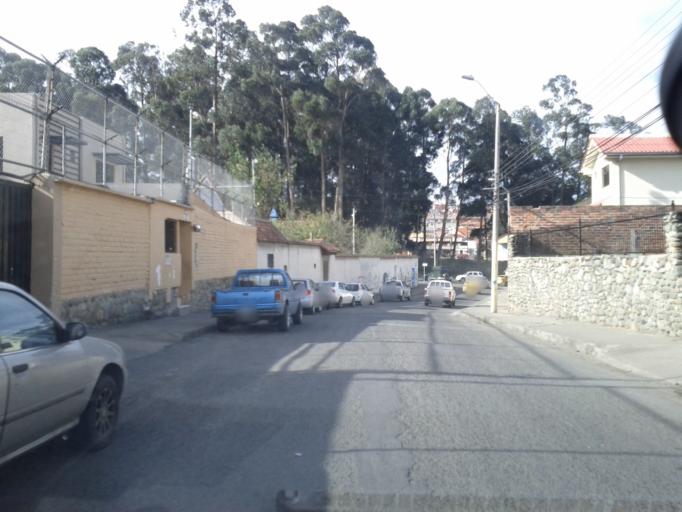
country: EC
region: Azuay
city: Cuenca
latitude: -2.8962
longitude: -79.0170
